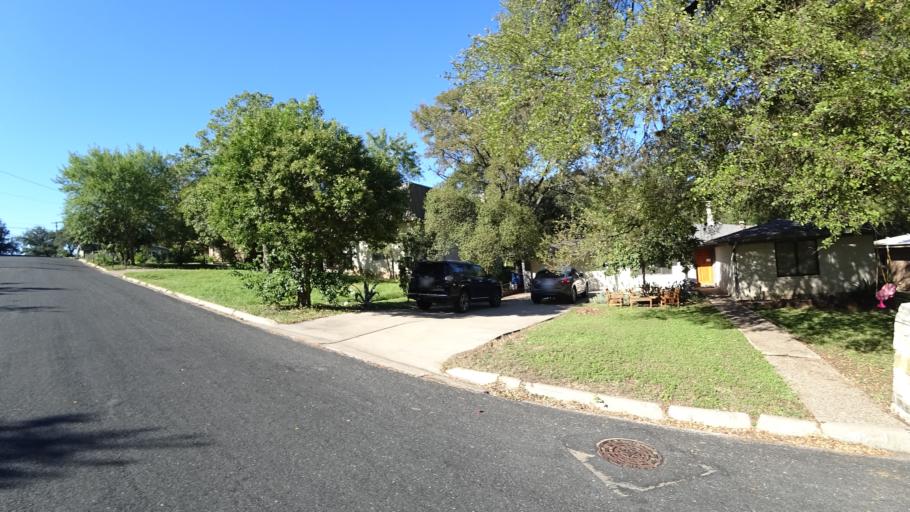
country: US
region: Texas
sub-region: Travis County
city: Austin
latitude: 30.2426
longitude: -97.7335
